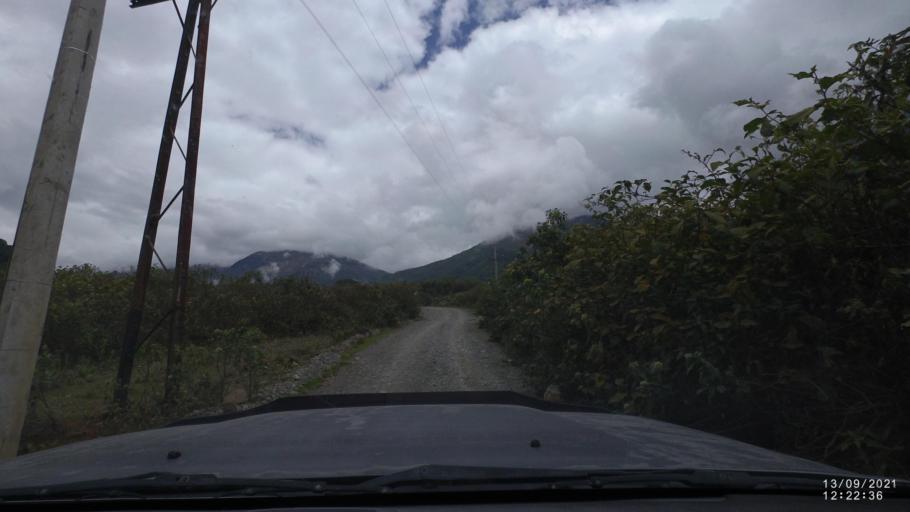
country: BO
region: Cochabamba
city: Colomi
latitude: -17.2394
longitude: -65.8179
